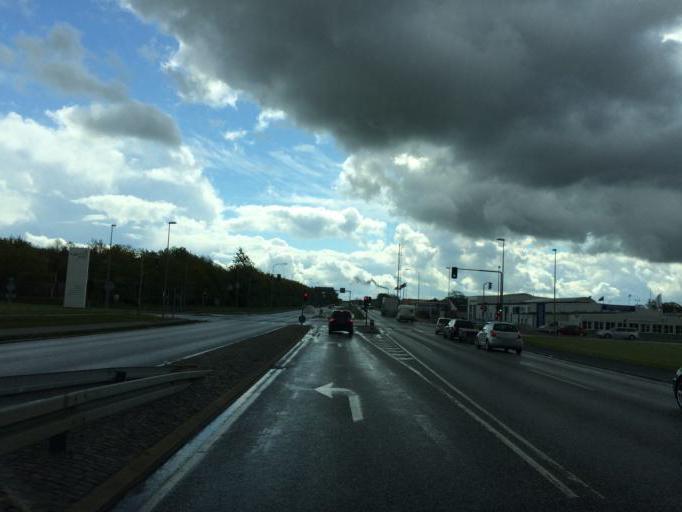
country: DK
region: Central Jutland
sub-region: Holstebro Kommune
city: Holstebro
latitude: 56.3729
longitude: 8.6260
